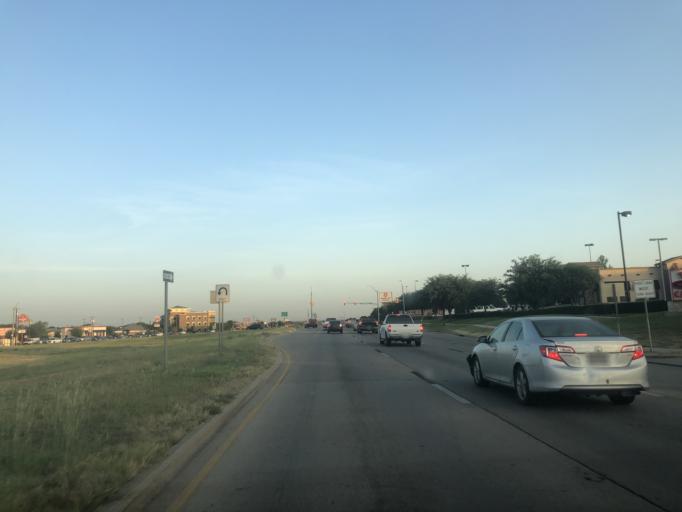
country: US
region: Texas
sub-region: Tarrant County
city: Lake Worth
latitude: 32.8112
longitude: -97.4298
